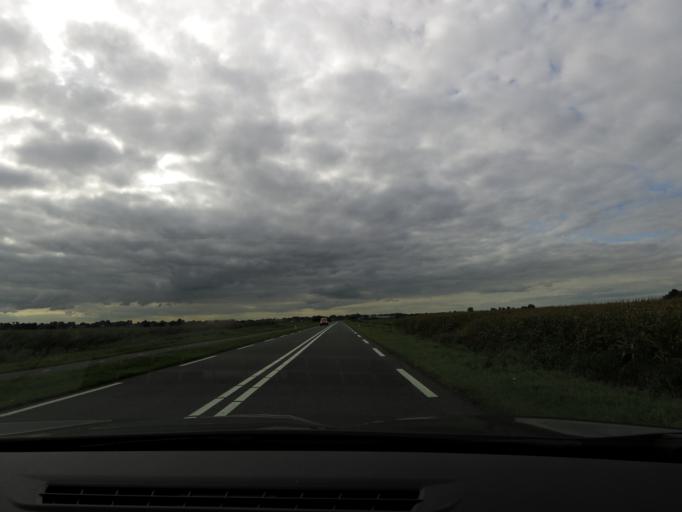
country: NL
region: South Holland
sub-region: Gemeente Schoonhoven
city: Schoonhoven
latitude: 51.9533
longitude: 4.8842
